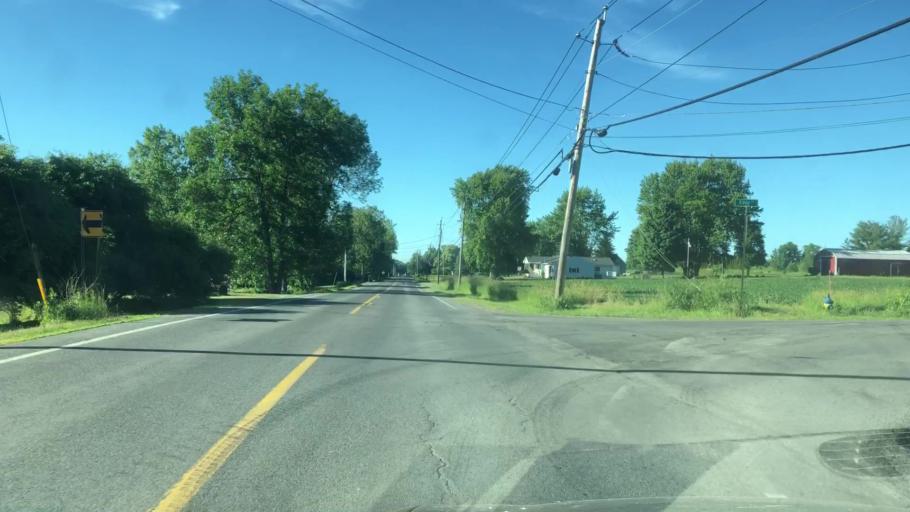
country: US
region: New York
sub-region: Wayne County
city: Macedon
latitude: 43.1163
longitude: -77.3209
